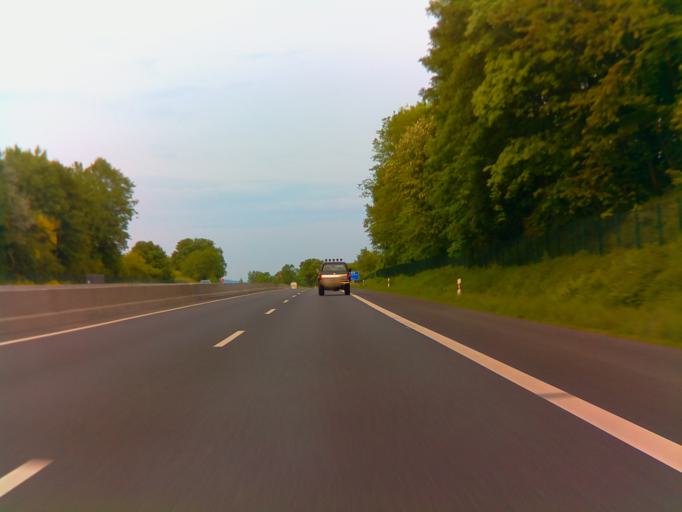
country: DE
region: Hesse
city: Gudensberg
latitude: 51.1869
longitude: 9.3829
